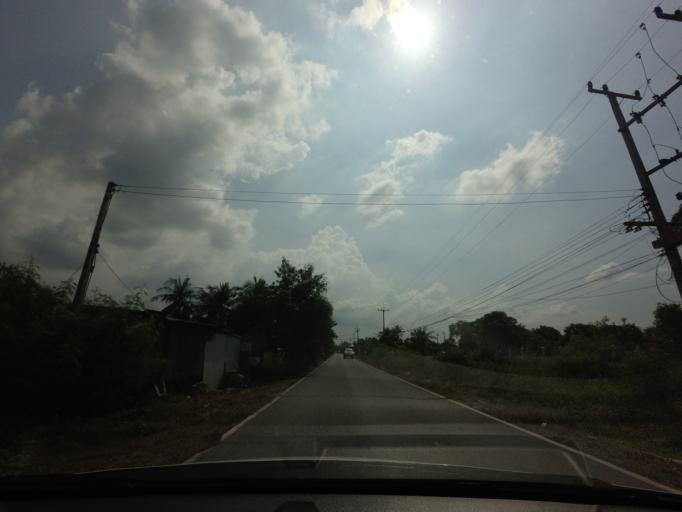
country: TH
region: Nakhon Pathom
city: Nakhon Chai Si
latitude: 13.8103
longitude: 100.1971
